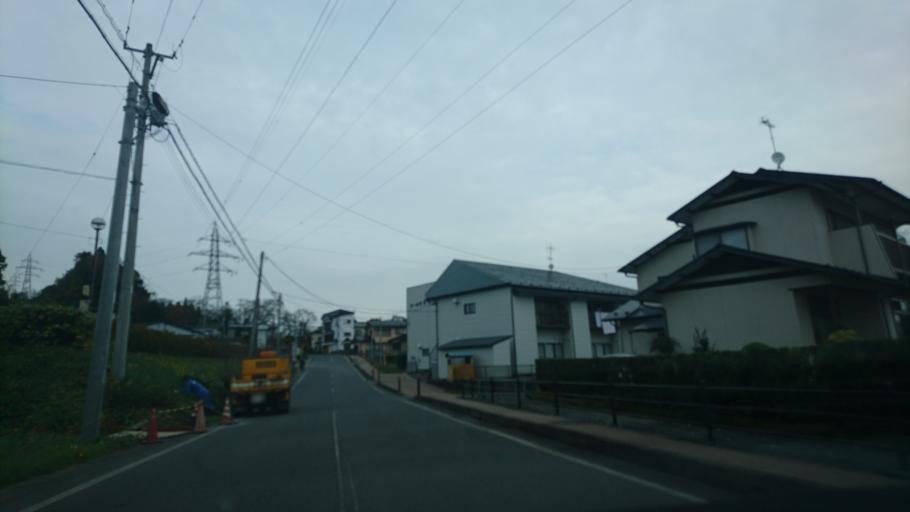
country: JP
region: Iwate
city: Ichinoseki
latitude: 38.9900
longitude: 141.1111
